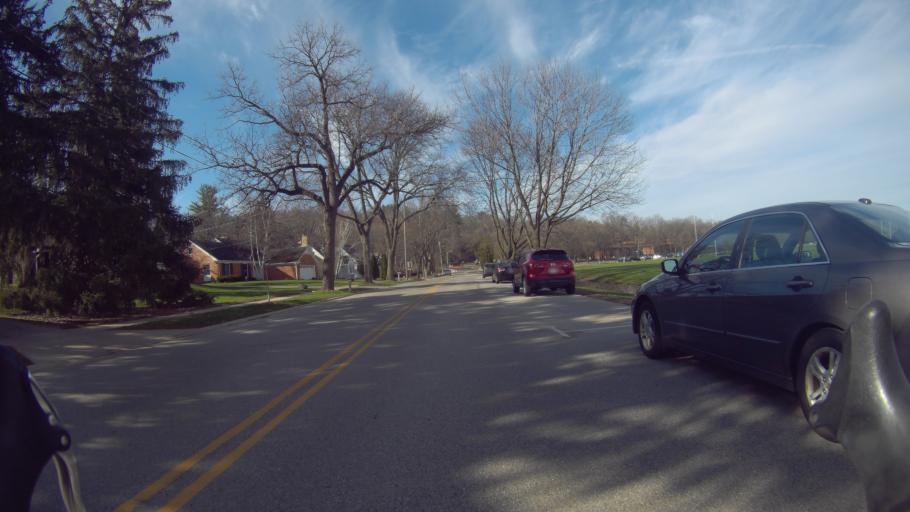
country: US
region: Wisconsin
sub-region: Dane County
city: Shorewood Hills
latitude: 43.0813
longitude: -89.4372
